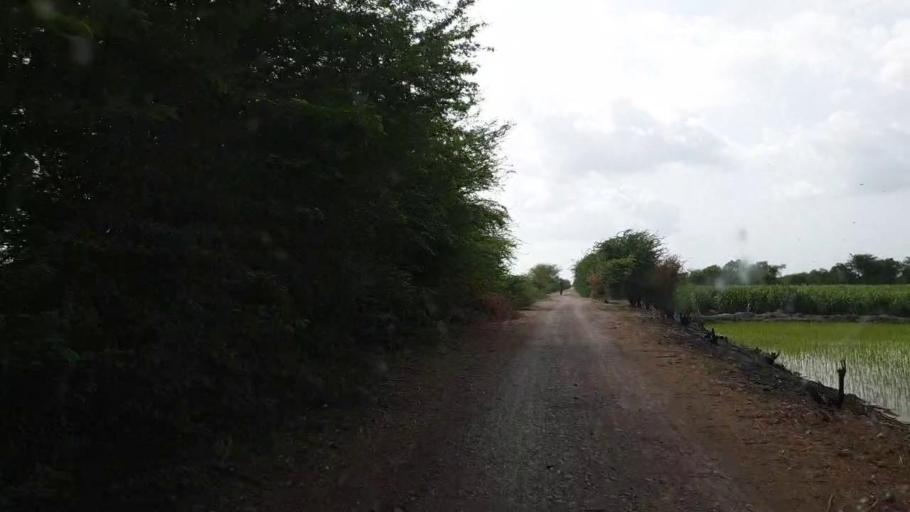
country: PK
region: Sindh
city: Kario
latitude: 24.6978
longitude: 68.6479
